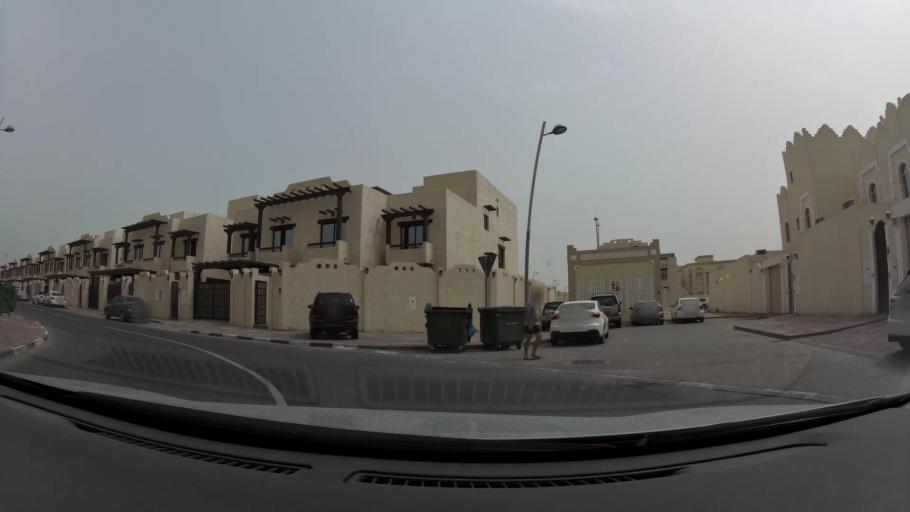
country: QA
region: Baladiyat ad Dawhah
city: Doha
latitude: 25.2329
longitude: 51.5469
